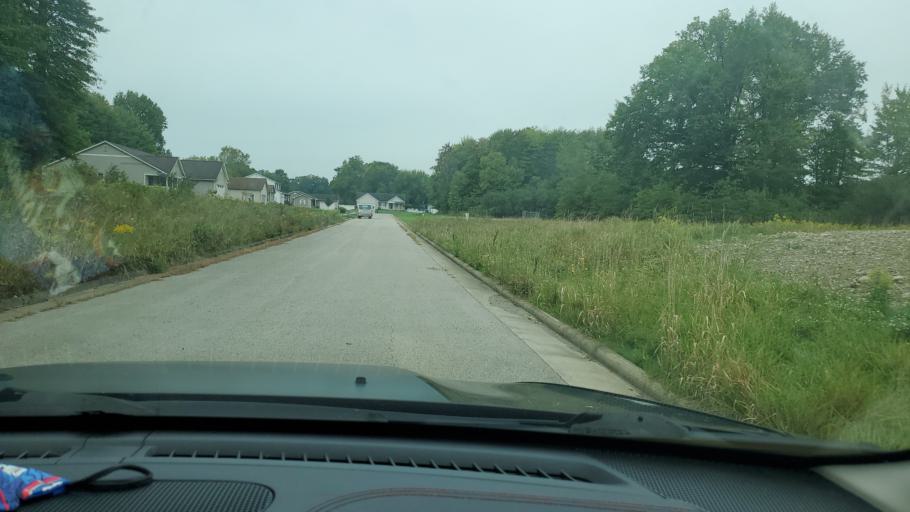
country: US
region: Ohio
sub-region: Mahoning County
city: Boardman
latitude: 41.0441
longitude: -80.6418
